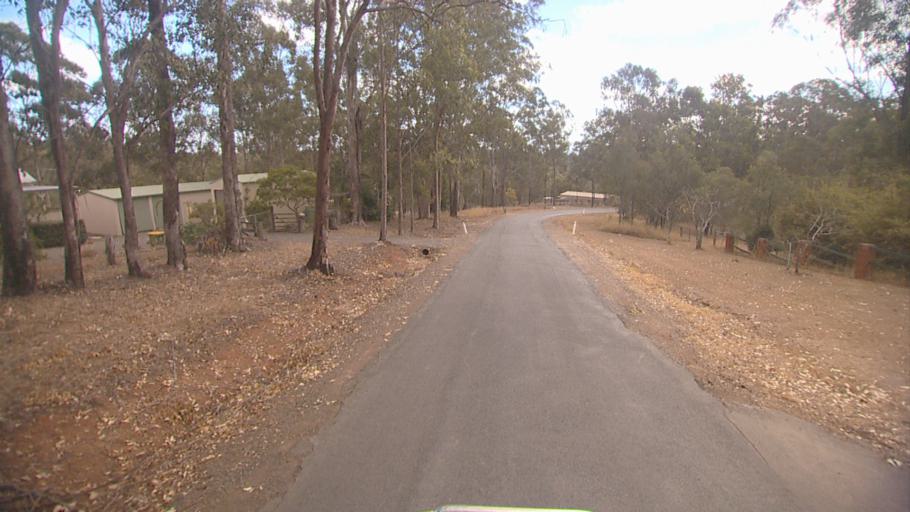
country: AU
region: Queensland
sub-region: Logan
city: Cedar Vale
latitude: -27.8898
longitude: 153.0298
